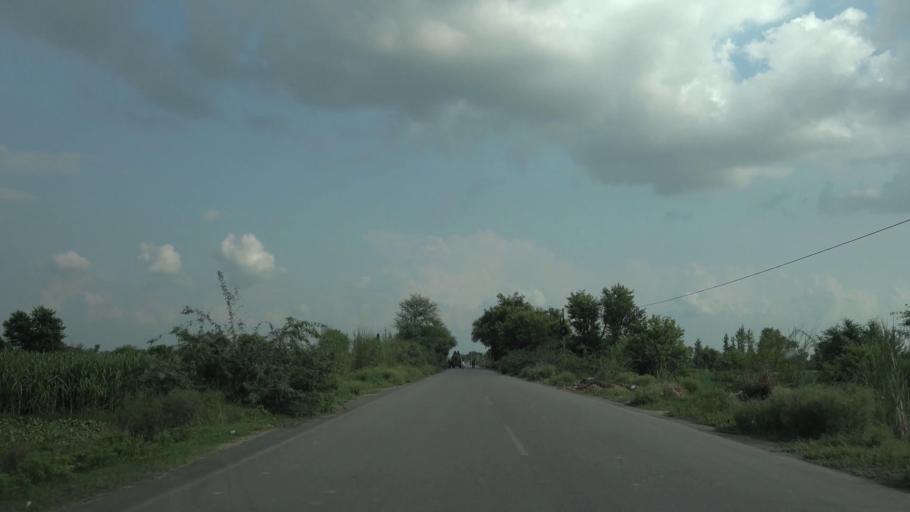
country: PK
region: Punjab
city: Nankana Sahib
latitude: 31.4892
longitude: 73.6069
